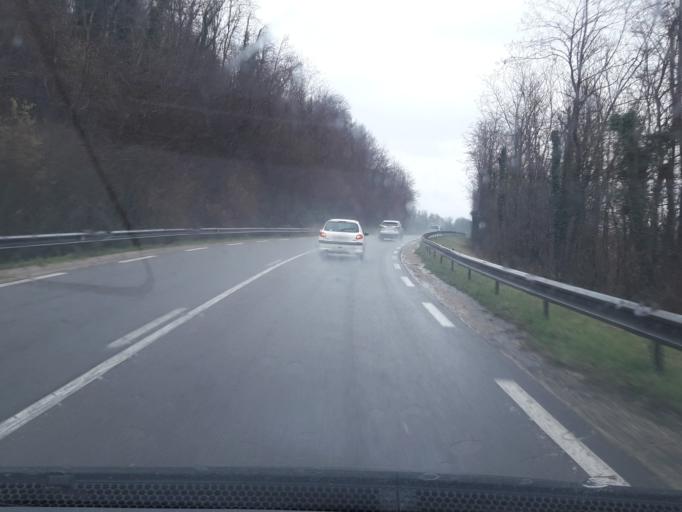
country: FR
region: Rhone-Alpes
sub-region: Departement de l'Ain
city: Belley
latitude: 45.7435
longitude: 5.7076
